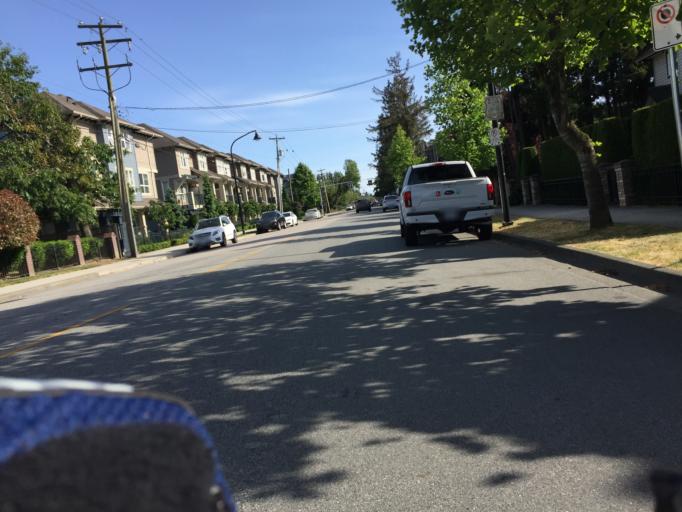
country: CA
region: British Columbia
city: Richmond
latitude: 49.1586
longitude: -123.1310
